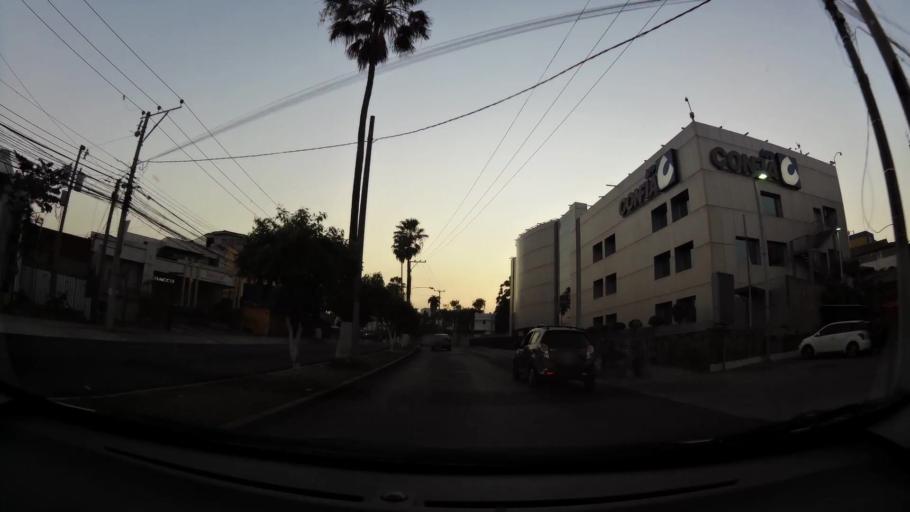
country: SV
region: San Salvador
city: San Salvador
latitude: 13.7004
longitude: -89.2251
